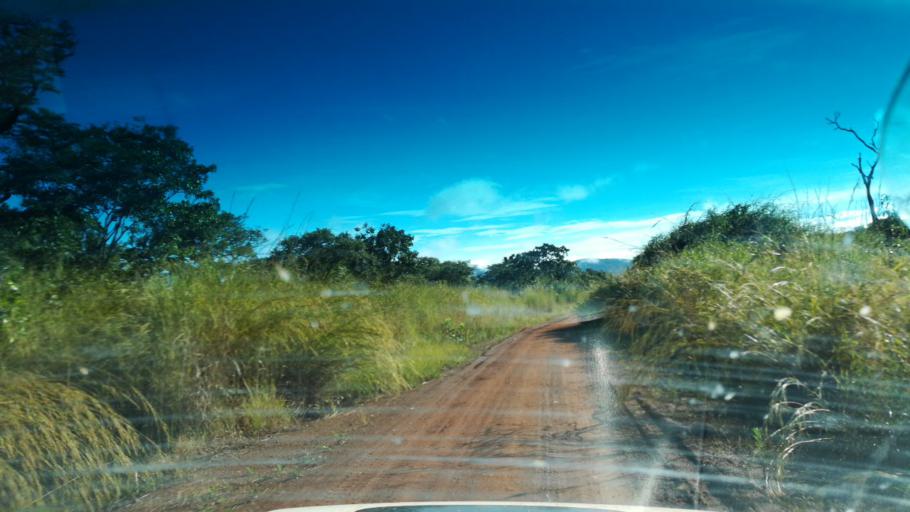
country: ZM
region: Northern
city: Kaputa
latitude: -8.2602
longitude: 29.0262
